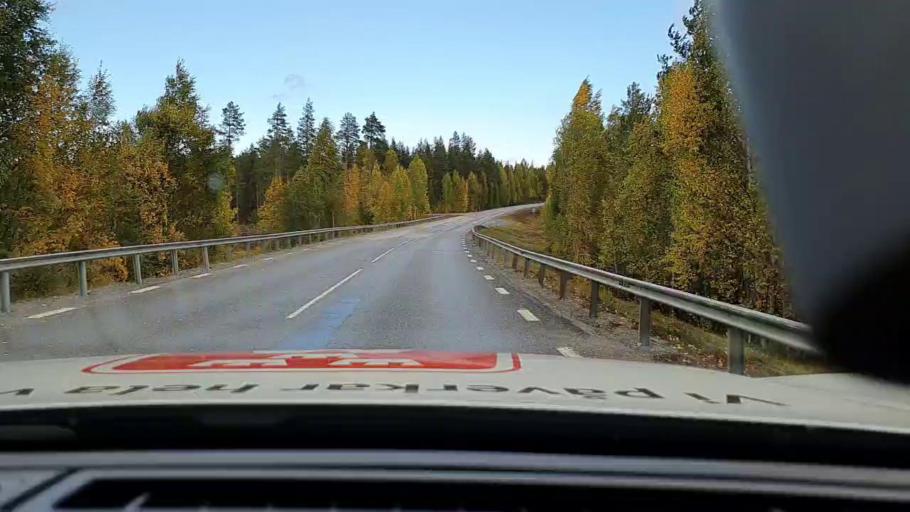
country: SE
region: Vaesterbotten
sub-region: Norsjo Kommun
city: Norsjoe
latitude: 64.9616
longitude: 19.6955
